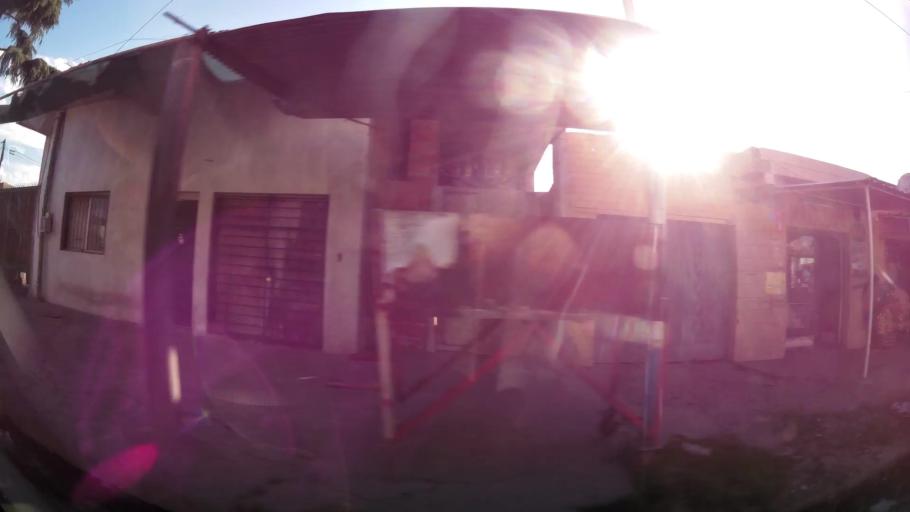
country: AR
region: Buenos Aires
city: Santa Catalina - Dique Lujan
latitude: -34.4987
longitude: -58.7283
